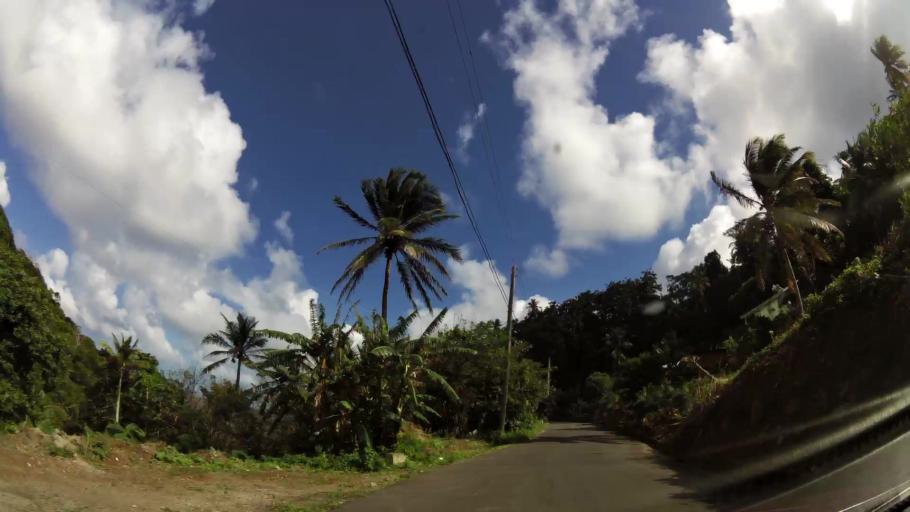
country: DM
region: Saint Andrew
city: Calibishie
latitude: 15.6157
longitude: -61.4080
